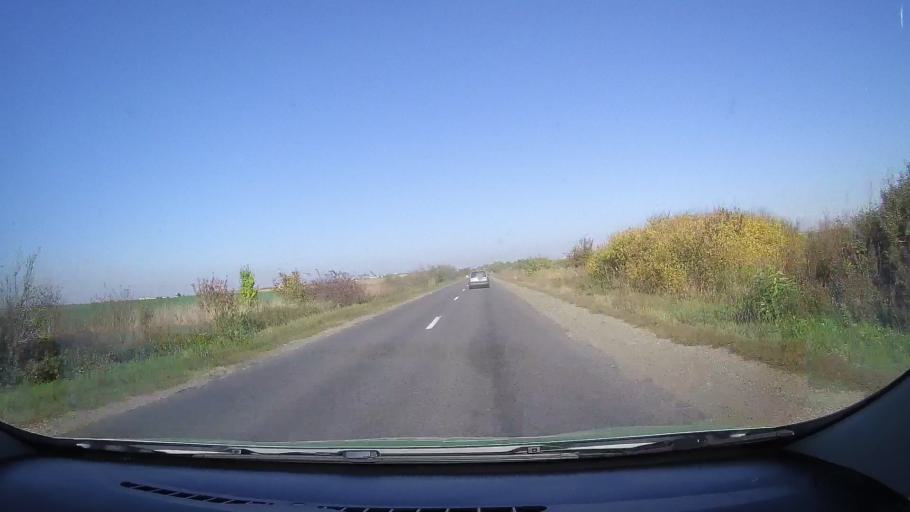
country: RO
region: Satu Mare
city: Carei
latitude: 47.6641
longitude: 22.4912
